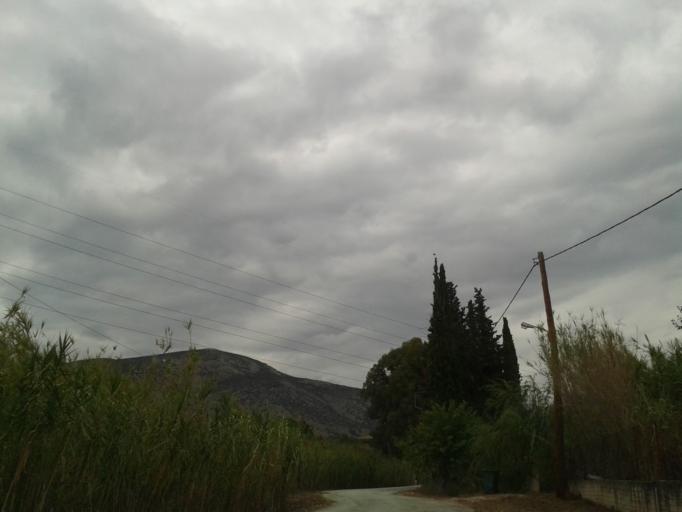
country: GR
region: Peloponnese
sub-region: Nomos Argolidos
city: Nea Kios
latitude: 37.5963
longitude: 22.7043
